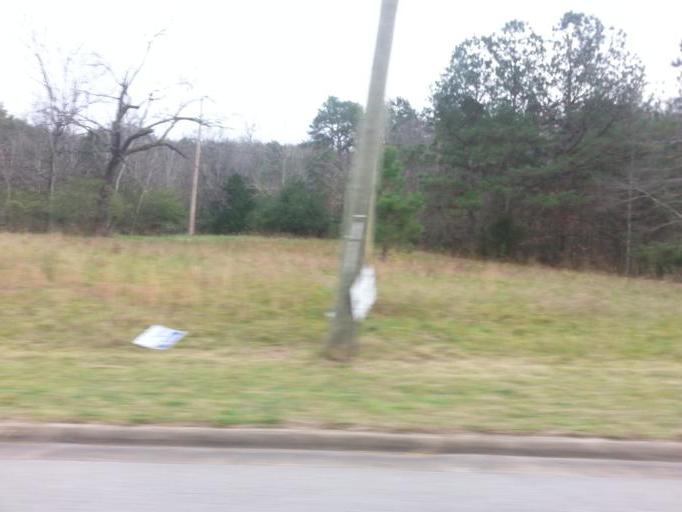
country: US
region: Tennessee
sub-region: Hamilton County
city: Sale Creek
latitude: 35.3726
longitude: -85.1142
